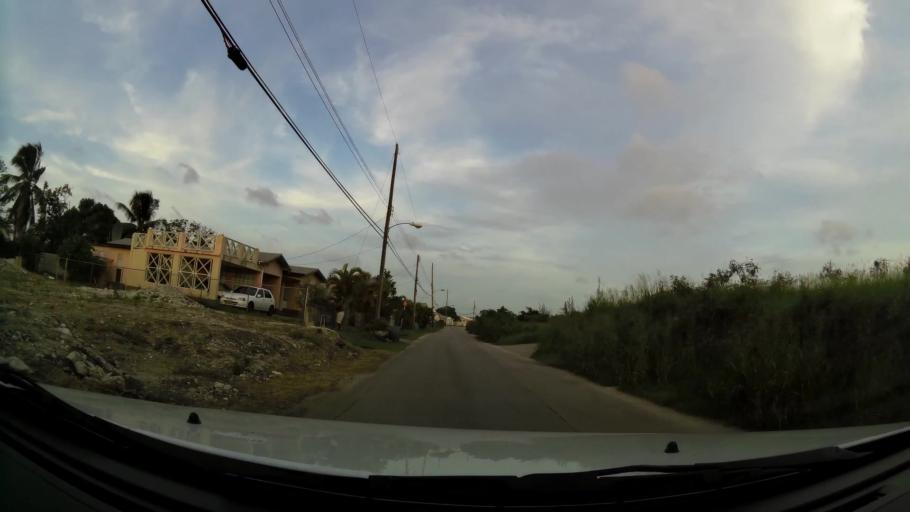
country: BB
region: Christ Church
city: Oistins
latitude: 13.0968
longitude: -59.4970
